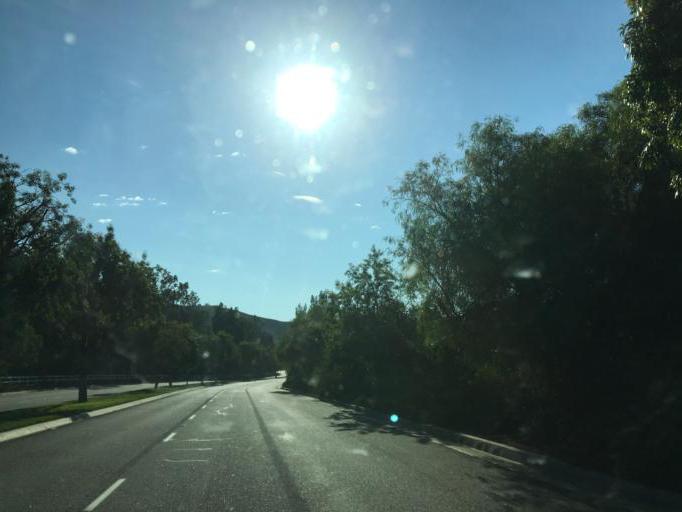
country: US
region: California
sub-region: Los Angeles County
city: Hidden Hills
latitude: 34.1522
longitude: -118.6852
